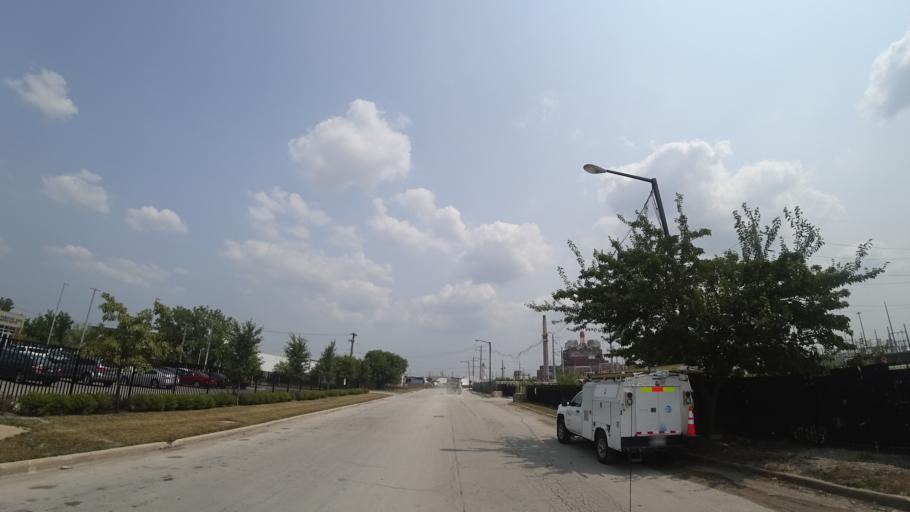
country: US
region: Illinois
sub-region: Cook County
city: Cicero
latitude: 41.8307
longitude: -87.7305
